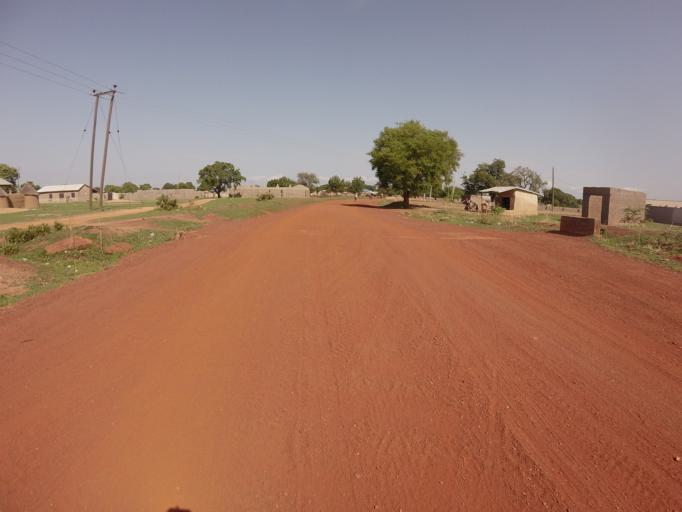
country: GH
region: Upper East
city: Bawku
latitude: 10.8305
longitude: -0.1699
